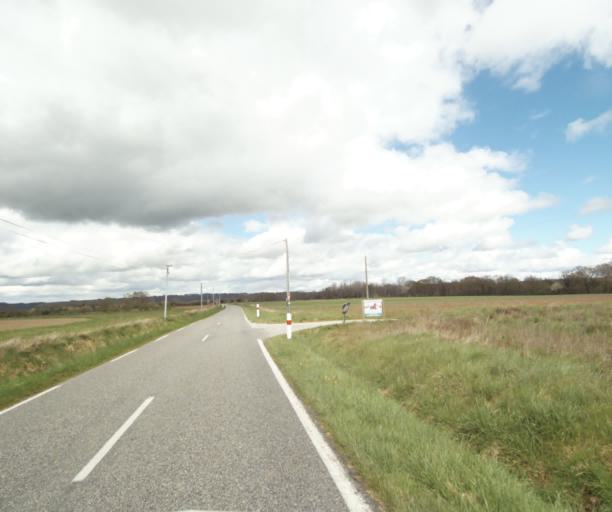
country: FR
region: Midi-Pyrenees
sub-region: Departement de la Haute-Garonne
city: Calmont
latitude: 43.2526
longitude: 1.6369
